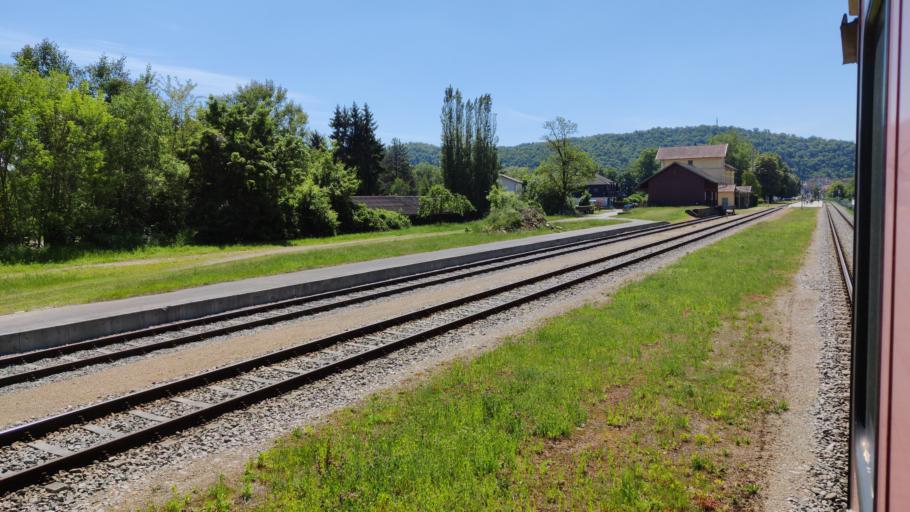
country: AT
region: Lower Austria
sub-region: Politischer Bezirk Horn
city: Gars am Kamp
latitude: 48.5991
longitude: 15.6546
